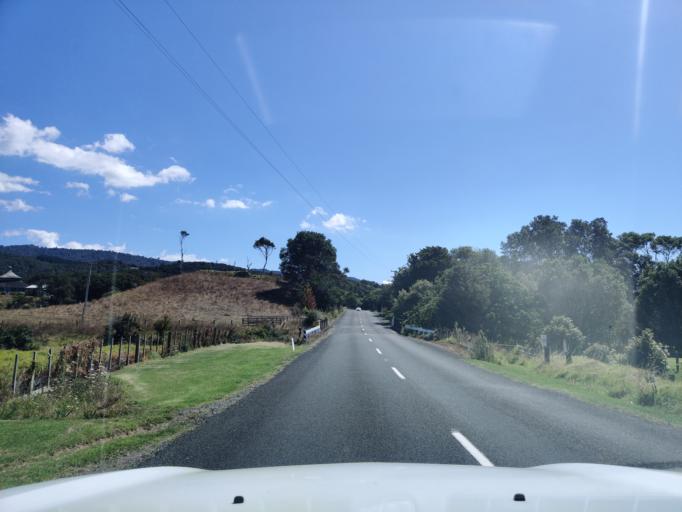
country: NZ
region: Waikato
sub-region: Thames-Coromandel District
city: Thames
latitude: -37.0438
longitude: 175.2970
